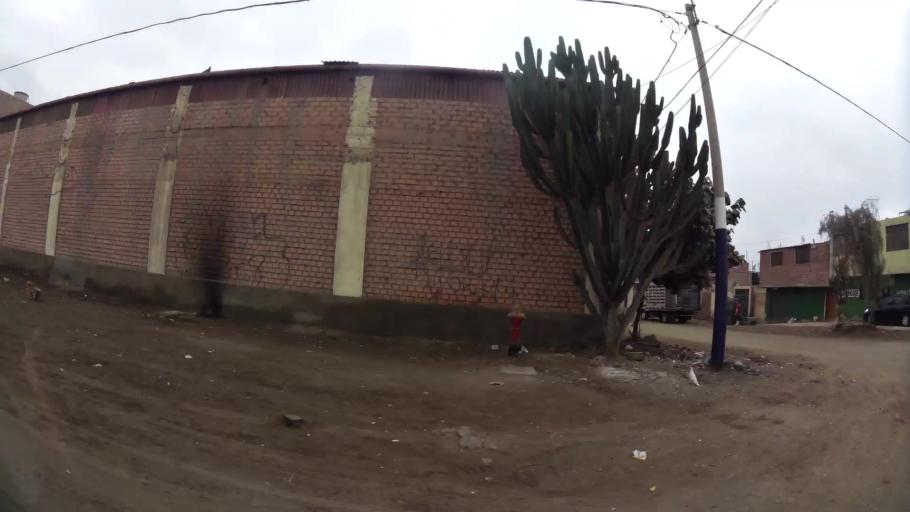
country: PE
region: Lima
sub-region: Lima
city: Surco
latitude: -12.1986
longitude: -77.0008
